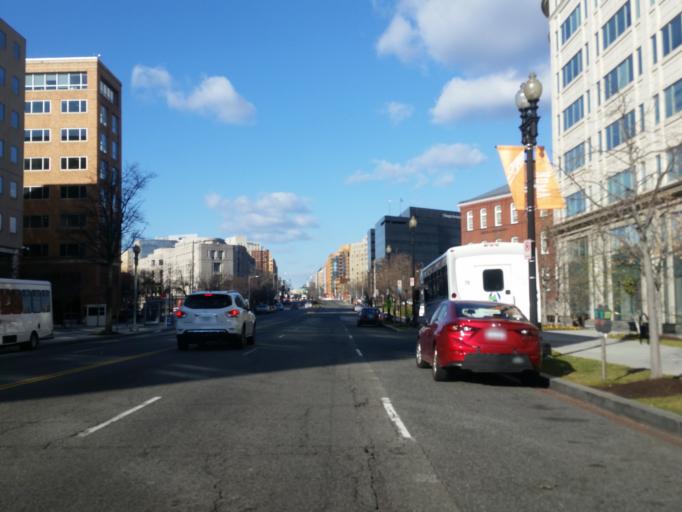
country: US
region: Washington, D.C.
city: Washington, D.C.
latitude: 38.8980
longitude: -77.0102
